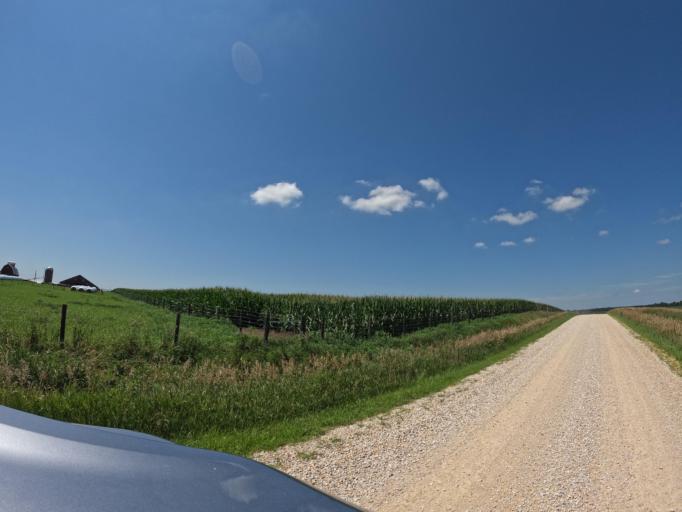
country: US
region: Iowa
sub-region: Clinton County
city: De Witt
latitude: 41.7793
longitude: -90.4062
